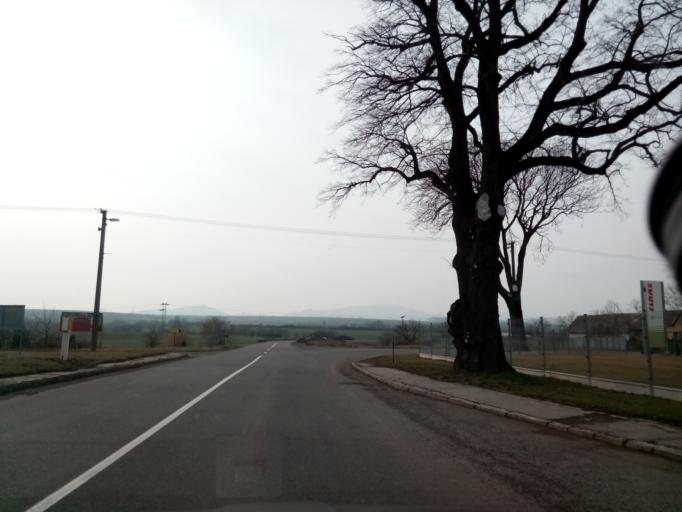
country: SK
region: Kosicky
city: Trebisov
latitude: 48.5573
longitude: 21.6712
